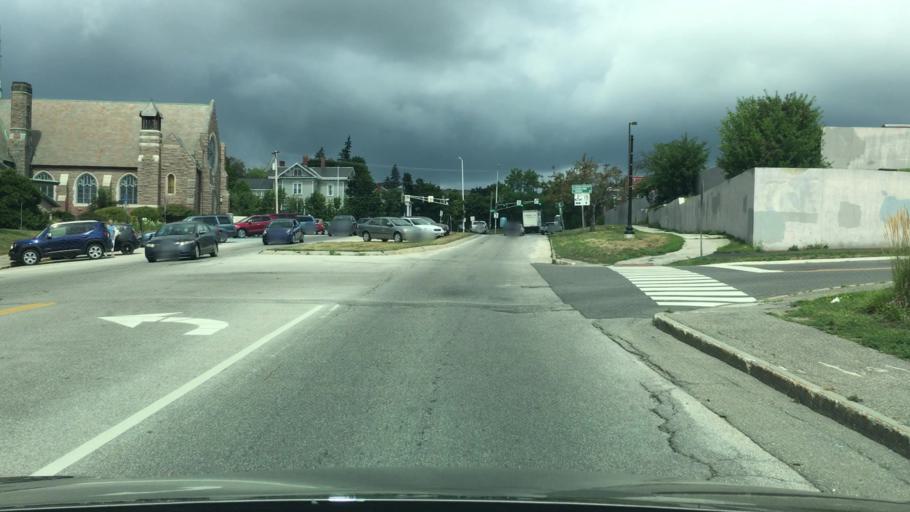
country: US
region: Maine
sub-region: Penobscot County
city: Brewer
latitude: 44.8019
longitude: -68.7670
